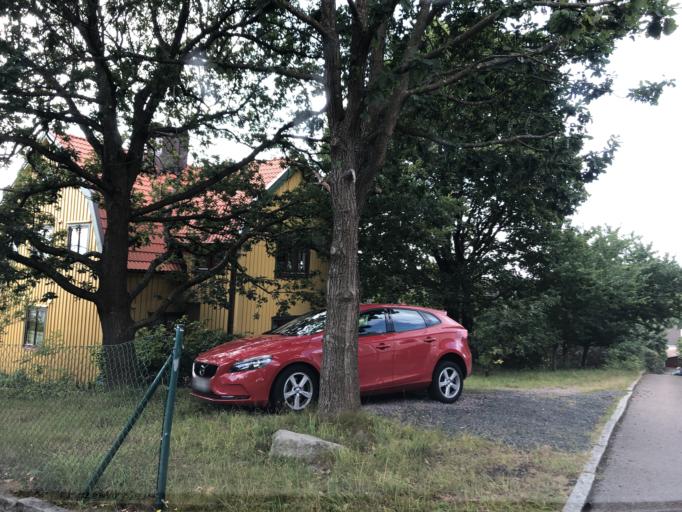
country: SE
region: Vaestra Goetaland
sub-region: Goteborg
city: Majorna
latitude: 57.7234
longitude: 11.9115
